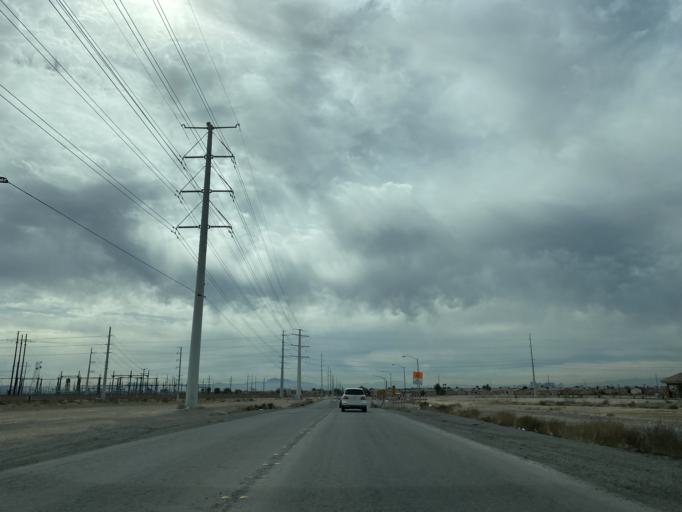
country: US
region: Nevada
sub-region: Clark County
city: Nellis Air Force Base
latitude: 36.2793
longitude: -115.0987
